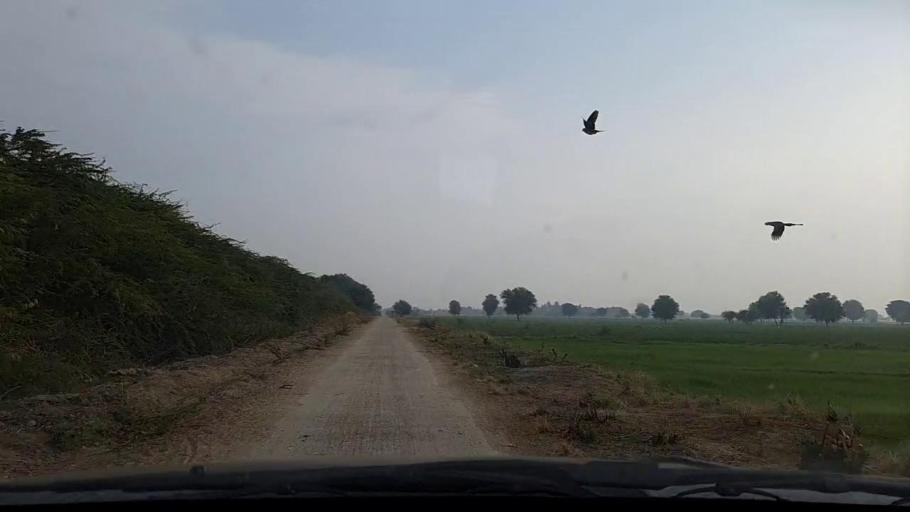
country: PK
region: Sindh
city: Pithoro
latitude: 25.7070
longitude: 69.3857
